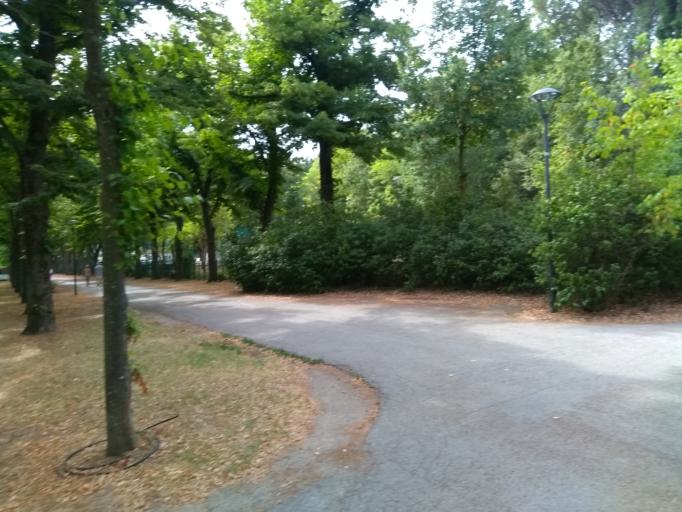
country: IT
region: Emilia-Romagna
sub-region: Provincia di Bologna
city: Imola
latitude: 44.3432
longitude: 11.7084
